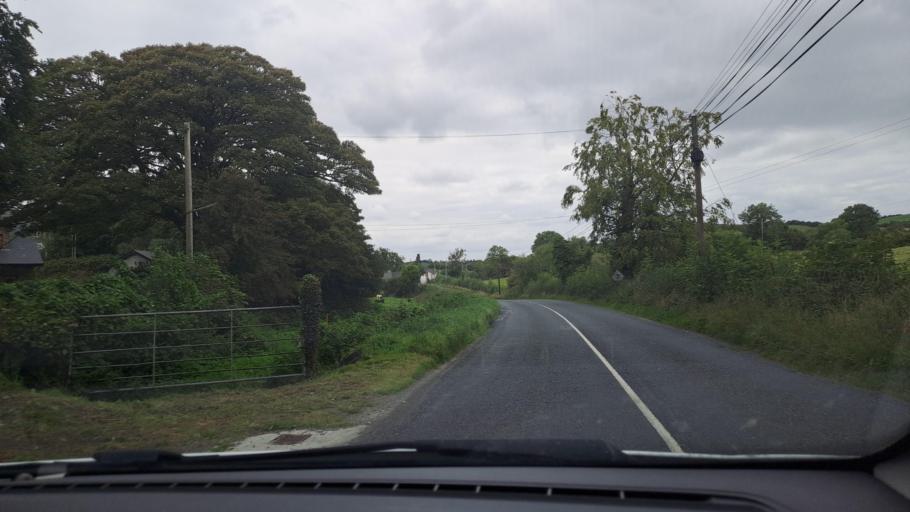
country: IE
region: Ulster
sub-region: An Cabhan
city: Bailieborough
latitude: 54.0103
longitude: -6.9212
